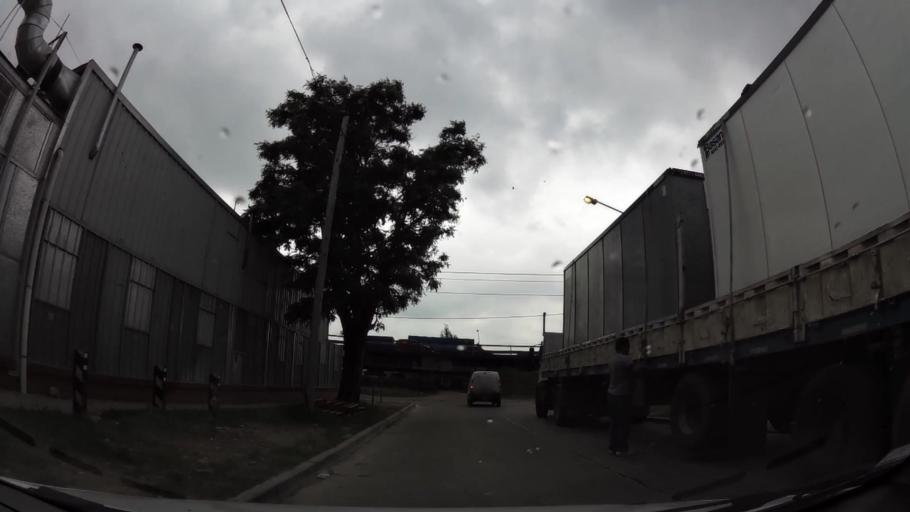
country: AR
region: Buenos Aires
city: San Justo
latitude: -34.7104
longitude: -58.5267
